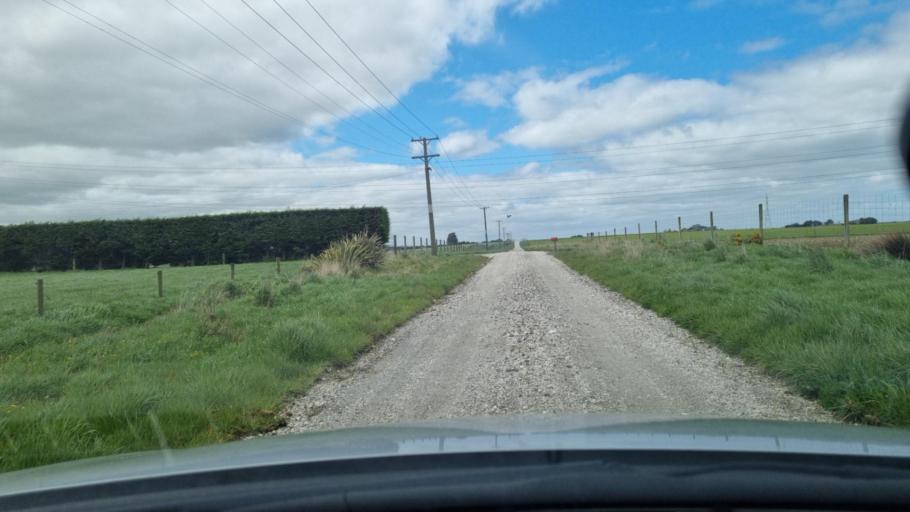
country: NZ
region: Southland
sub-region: Invercargill City
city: Invercargill
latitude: -46.4427
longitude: 168.4413
